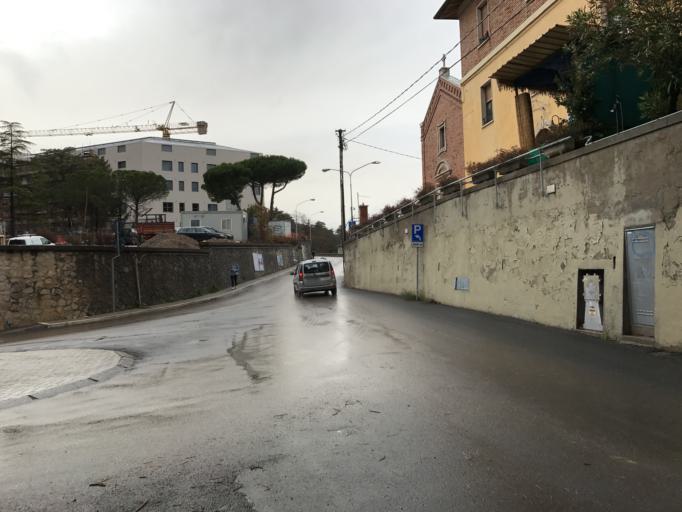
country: IT
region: Umbria
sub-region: Provincia di Perugia
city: Perugia
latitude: 43.1143
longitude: 12.4045
